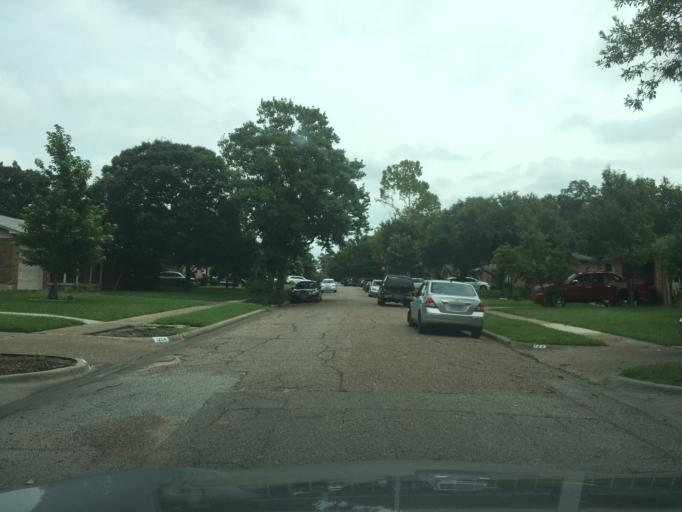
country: US
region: Texas
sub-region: Dallas County
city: Richardson
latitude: 32.9477
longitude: -96.7633
